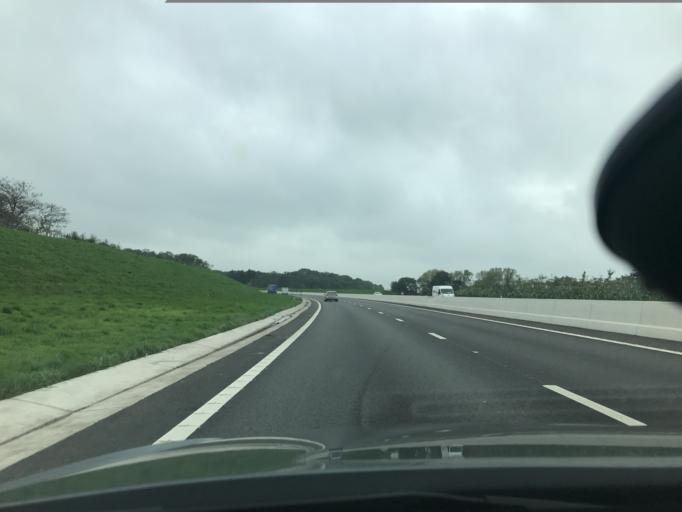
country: GB
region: England
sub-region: Cheshire East
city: Mere
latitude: 53.3321
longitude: -2.4215
